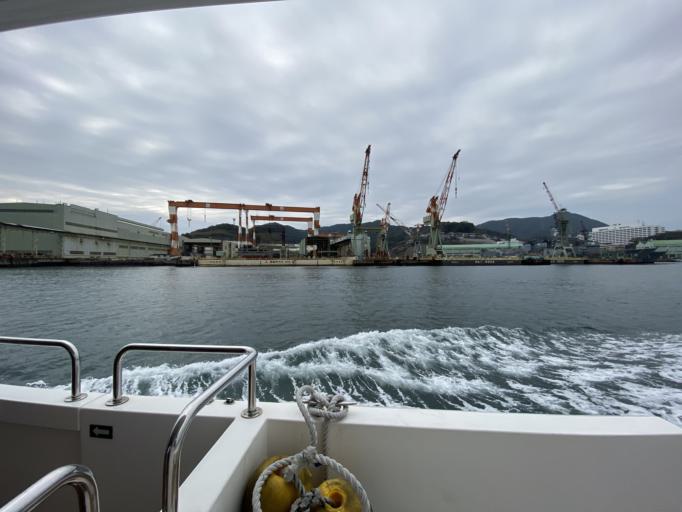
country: JP
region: Nagasaki
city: Nagasaki-shi
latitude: 32.7320
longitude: 129.8584
